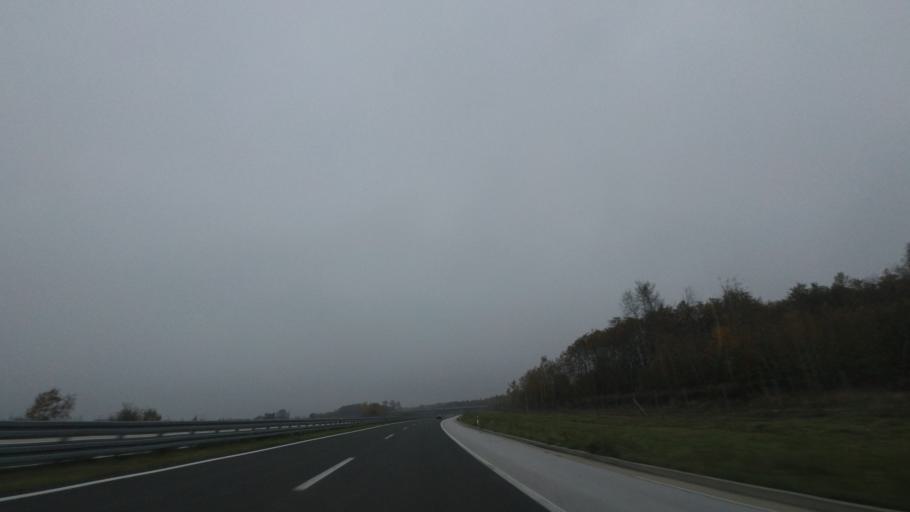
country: HR
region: Zagrebacka
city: Turopolje
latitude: 45.6108
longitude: 16.1175
